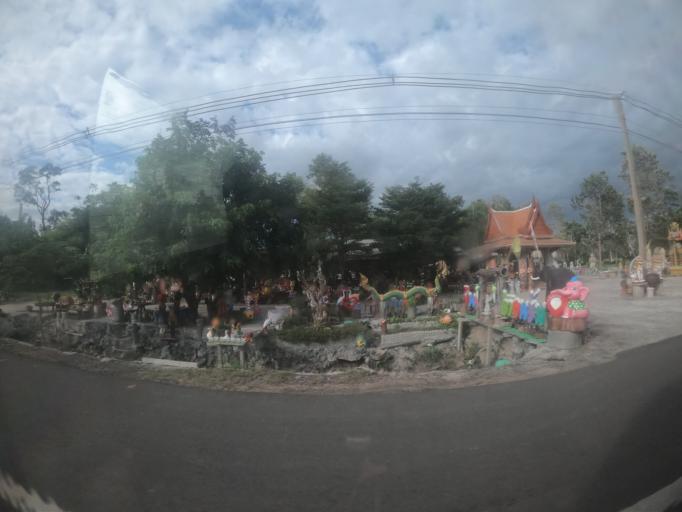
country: TH
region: Surin
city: Prasat
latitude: 14.5868
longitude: 103.4706
